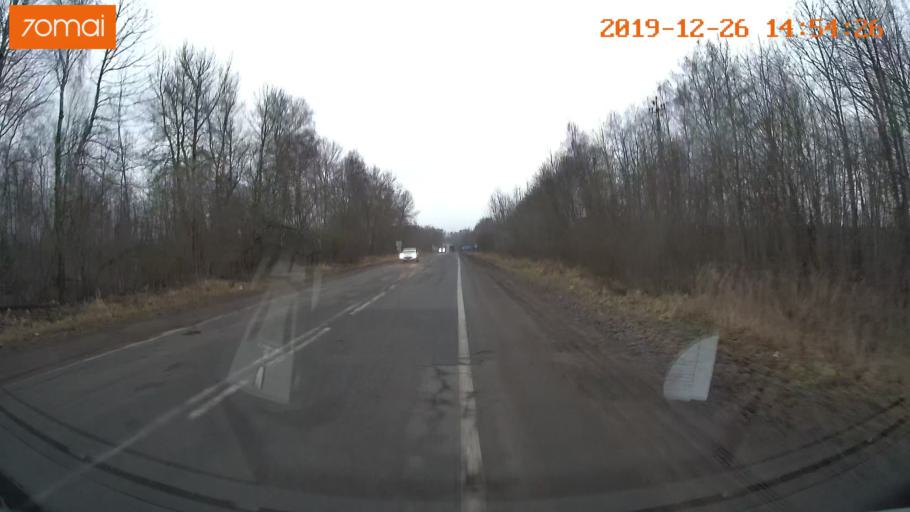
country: RU
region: Jaroslavl
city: Rybinsk
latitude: 58.3074
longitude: 38.8844
